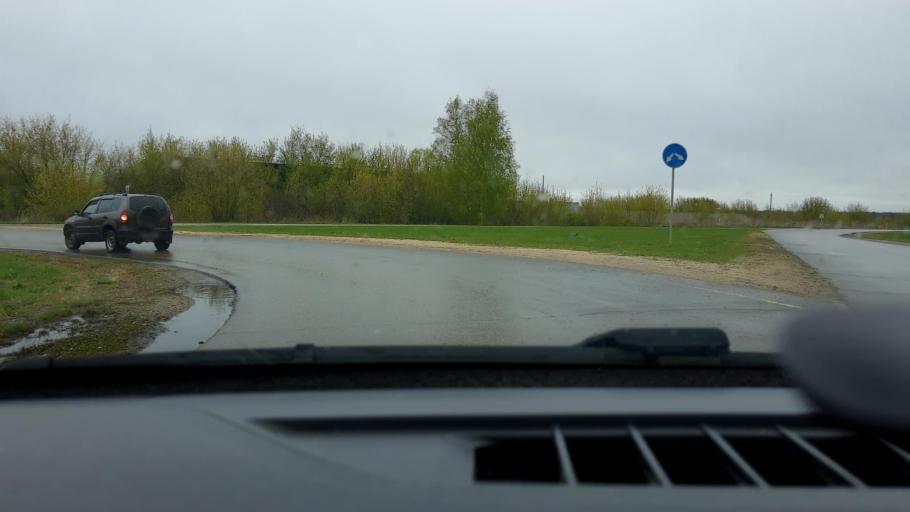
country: RU
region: Nizjnij Novgorod
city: Buturlino
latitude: 55.5723
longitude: 44.8562
